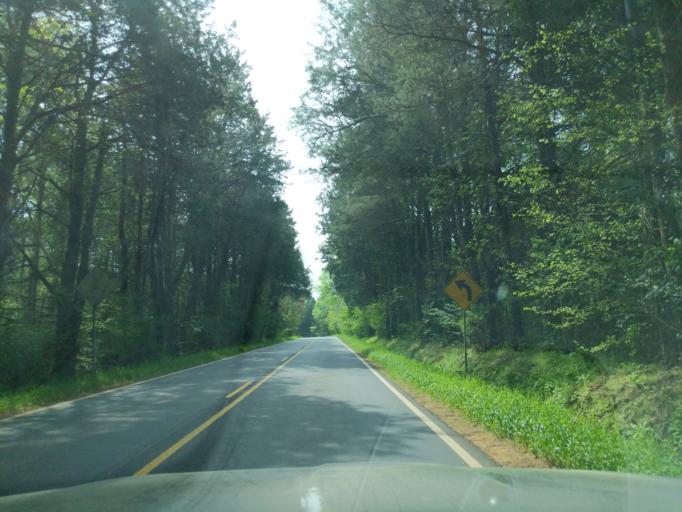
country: US
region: Georgia
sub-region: Columbia County
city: Appling
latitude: 33.6273
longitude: -82.3393
